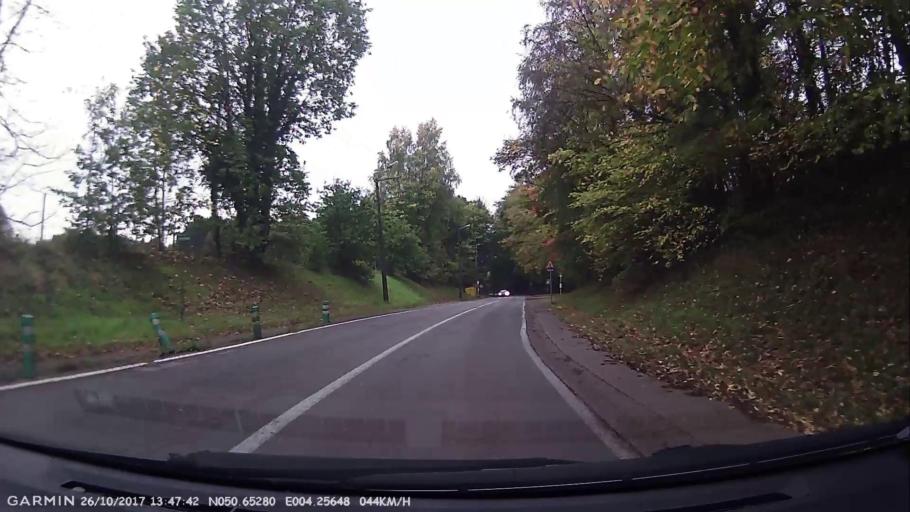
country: BE
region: Wallonia
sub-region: Province du Brabant Wallon
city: Ittre
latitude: 50.6526
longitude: 4.2565
